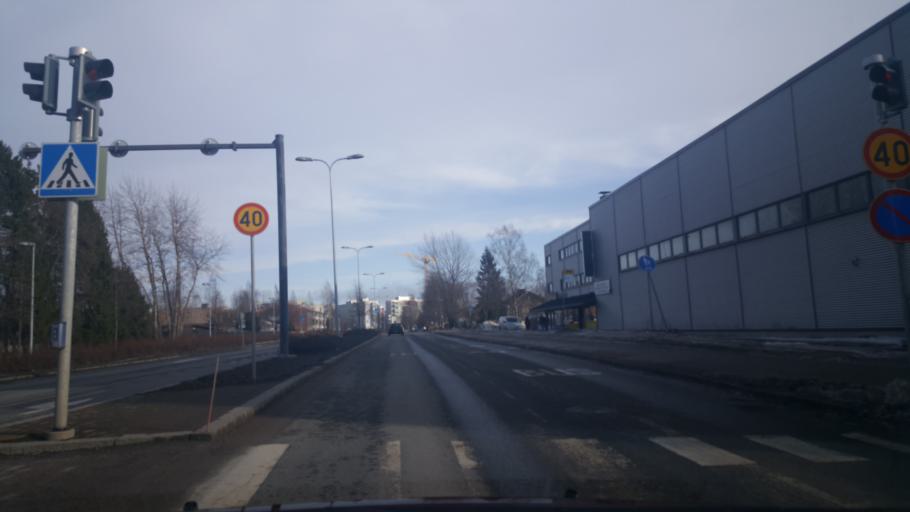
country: FI
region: Uusimaa
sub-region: Helsinki
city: Vantaa
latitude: 60.2907
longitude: 25.0231
